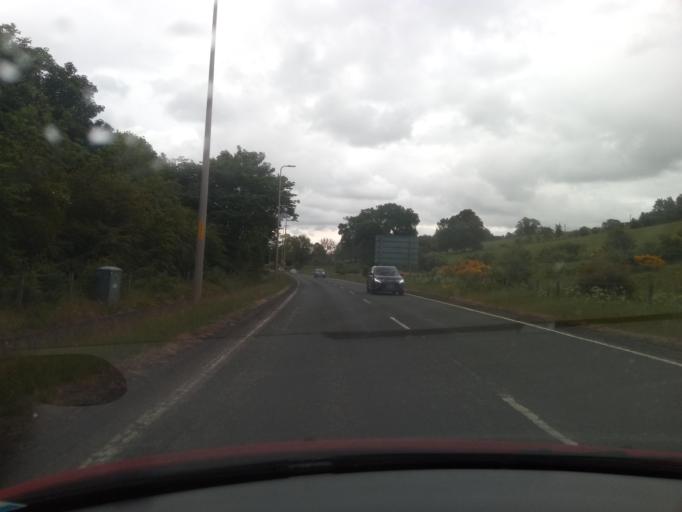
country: GB
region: Scotland
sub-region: The Scottish Borders
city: Galashiels
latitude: 55.6003
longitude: -2.7693
